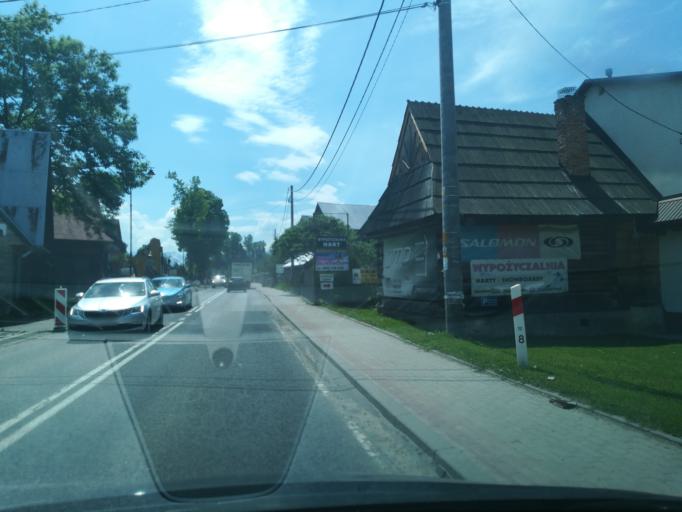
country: PL
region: Lesser Poland Voivodeship
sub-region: Powiat tatrzanski
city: Bialka Tatrzanska
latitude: 49.3911
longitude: 20.1049
